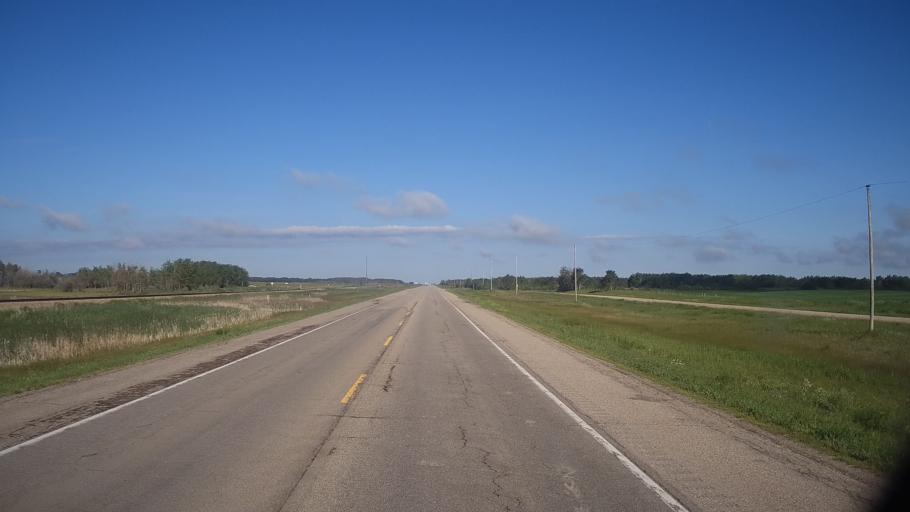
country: CA
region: Saskatchewan
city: Lanigan
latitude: 51.8523
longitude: -105.0715
